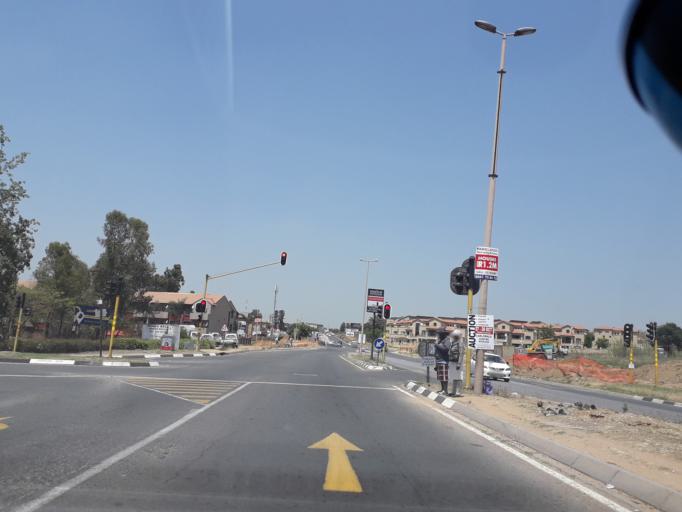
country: ZA
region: Gauteng
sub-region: City of Johannesburg Metropolitan Municipality
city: Midrand
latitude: -25.9683
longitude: 28.1208
